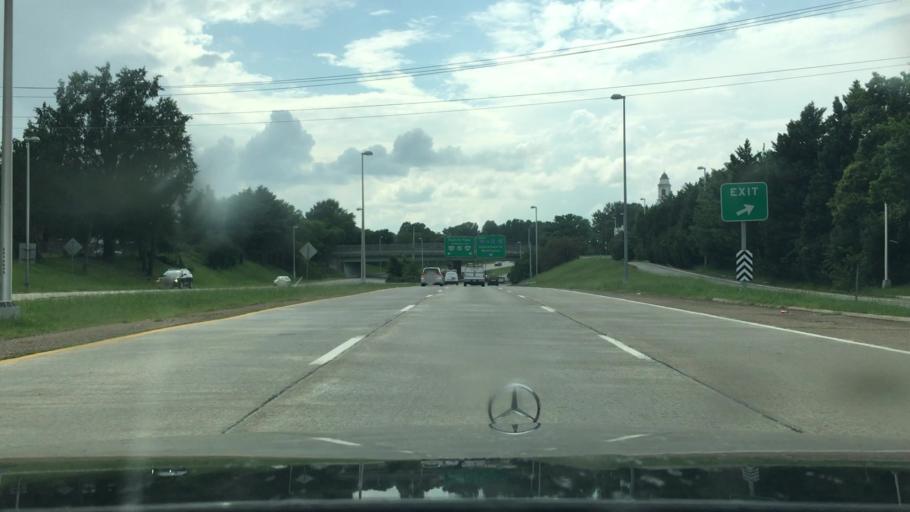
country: US
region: Virginia
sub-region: City of Richmond
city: Richmond
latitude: 37.5481
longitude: -77.4721
